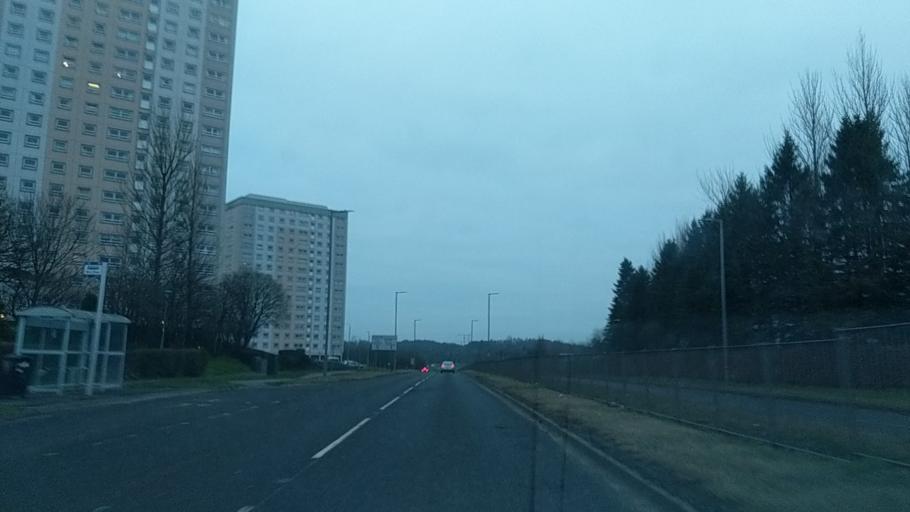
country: GB
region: Scotland
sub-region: South Lanarkshire
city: East Kilbride
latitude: 55.7555
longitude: -4.1602
